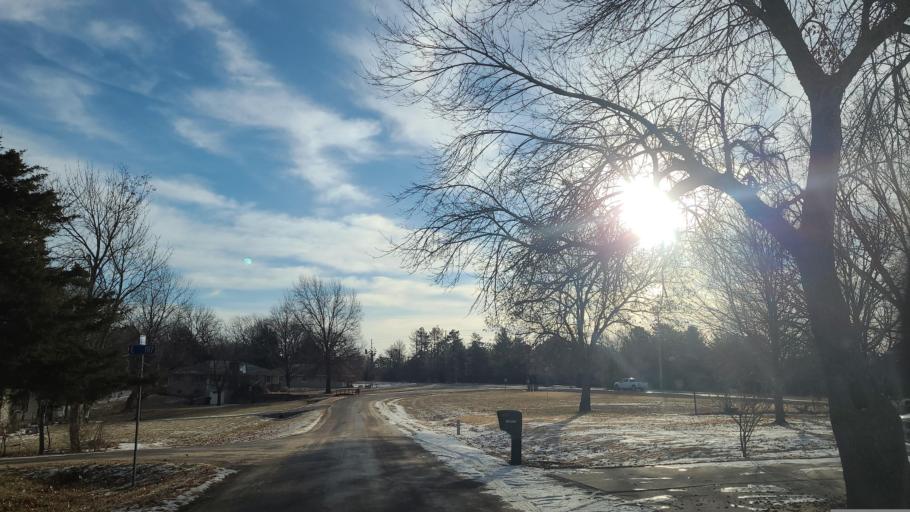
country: US
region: Kansas
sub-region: Douglas County
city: Lawrence
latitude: 38.9868
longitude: -95.2955
